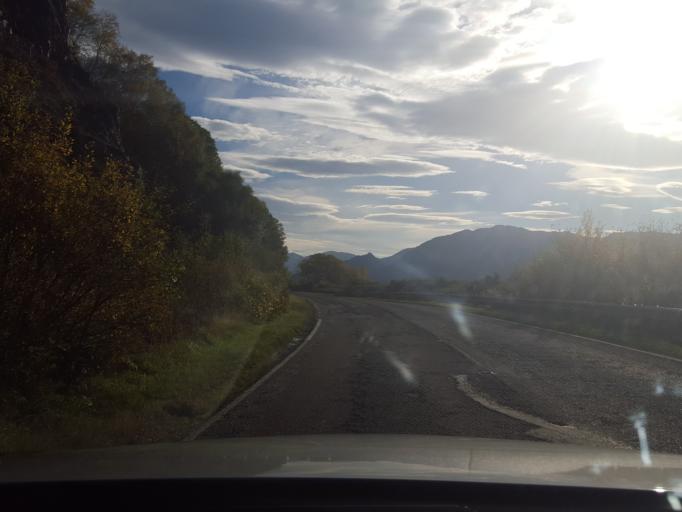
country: GB
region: Scotland
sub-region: Highland
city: Fort William
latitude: 57.2640
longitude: -5.5016
